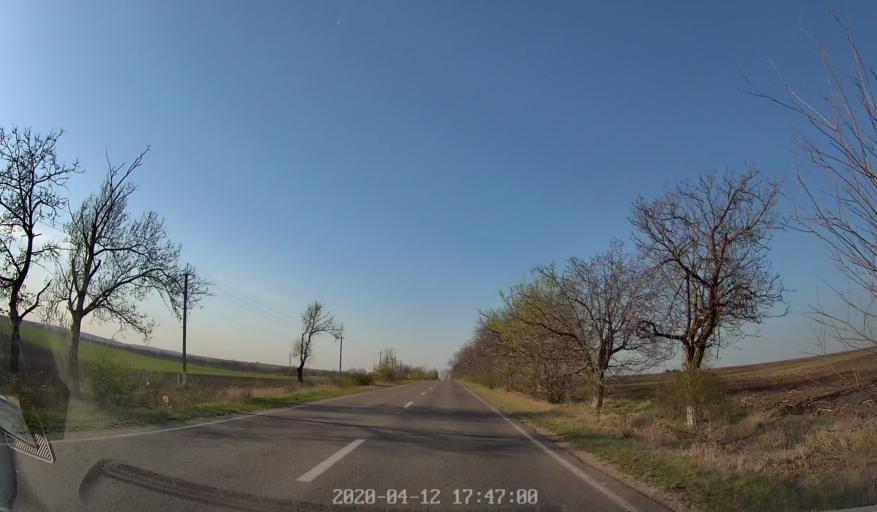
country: MD
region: Telenesti
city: Cocieri
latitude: 47.3759
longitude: 29.1097
